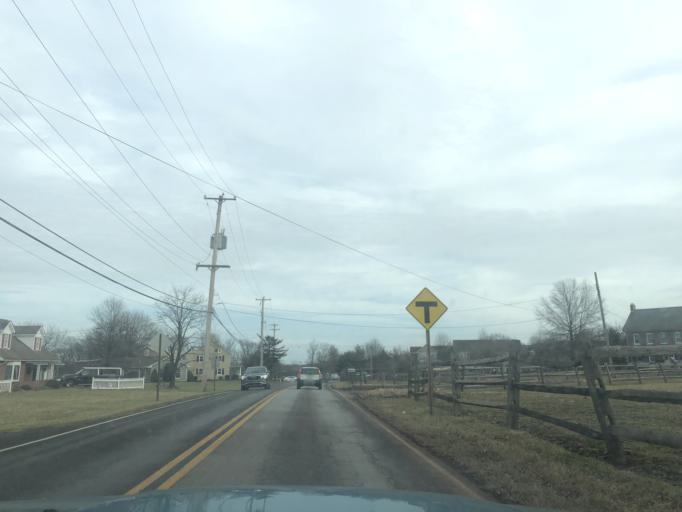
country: US
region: Pennsylvania
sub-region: Montgomery County
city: Harleysville
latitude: 40.2770
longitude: -75.3988
